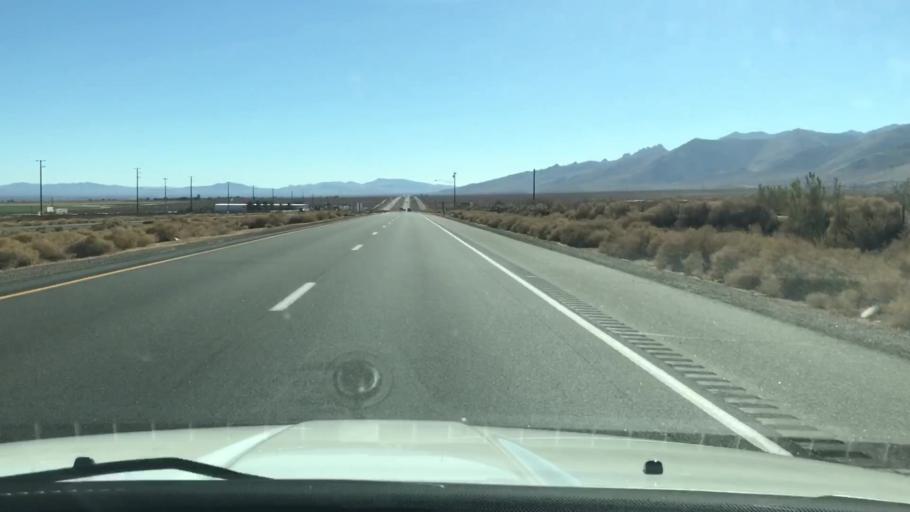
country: US
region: California
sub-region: Kern County
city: Inyokern
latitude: 35.8102
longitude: -117.8736
